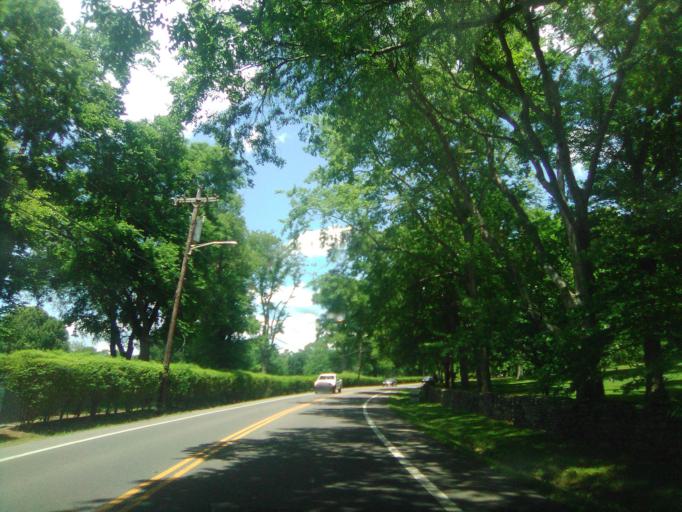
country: US
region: Tennessee
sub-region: Davidson County
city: Belle Meade
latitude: 36.1221
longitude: -86.8592
